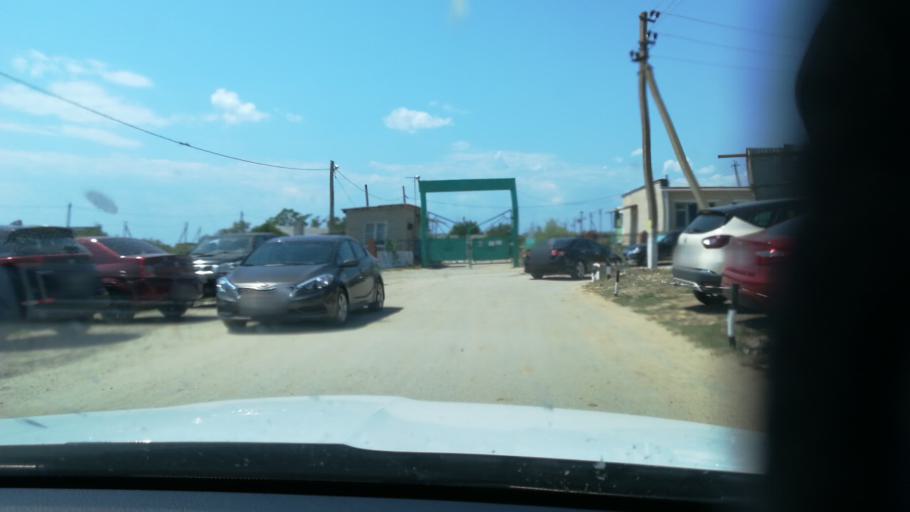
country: RU
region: Krasnodarskiy
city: Vyshestebliyevskaya
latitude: 45.1124
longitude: 36.8772
